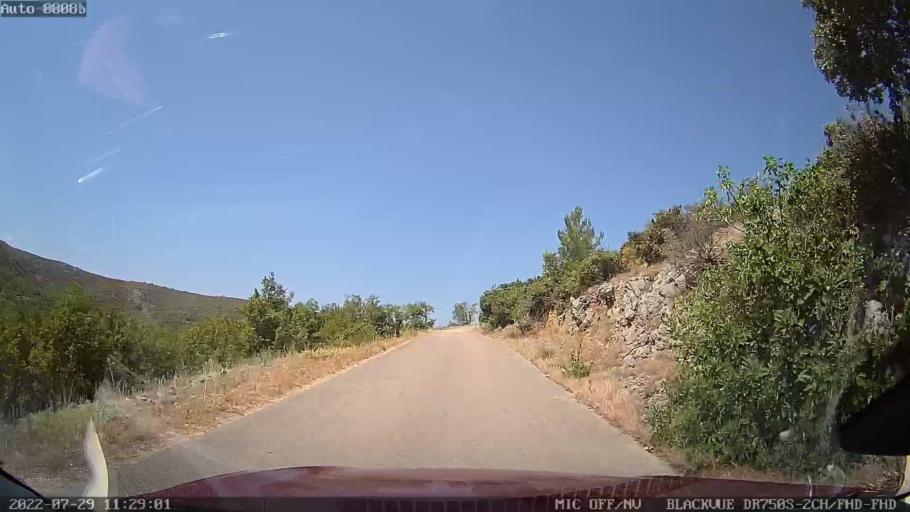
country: HR
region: Zadarska
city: Obrovac
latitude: 44.1942
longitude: 15.7587
